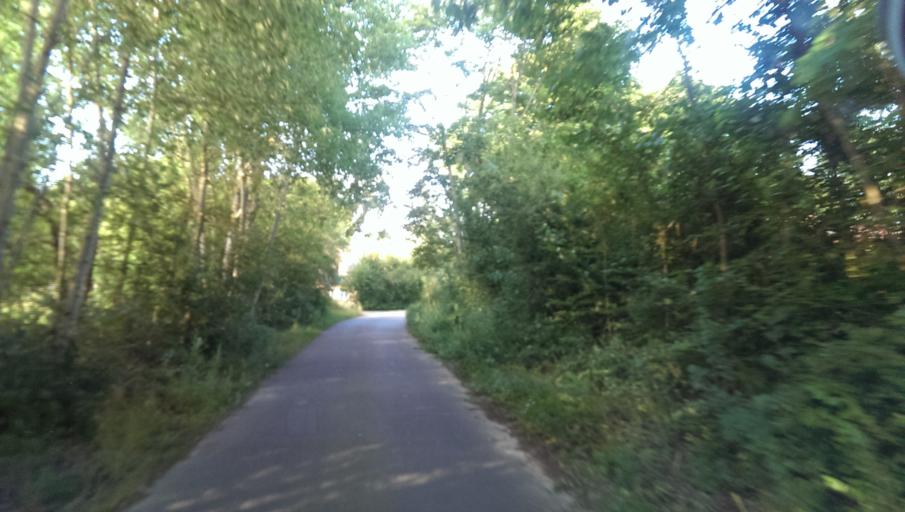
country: DE
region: Brandenburg
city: Treuenbrietzen
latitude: 52.0391
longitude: 12.8636
